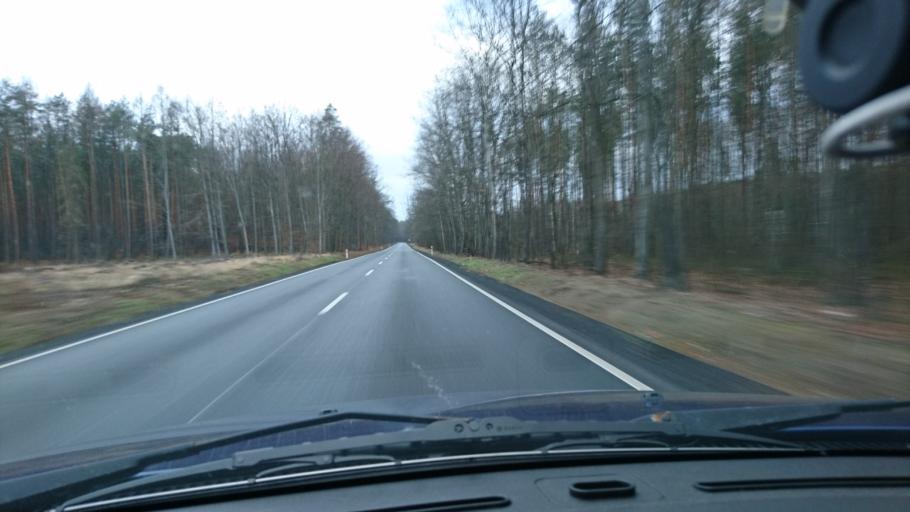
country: PL
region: Opole Voivodeship
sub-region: Powiat oleski
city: Olesno
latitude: 50.9315
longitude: 18.3333
